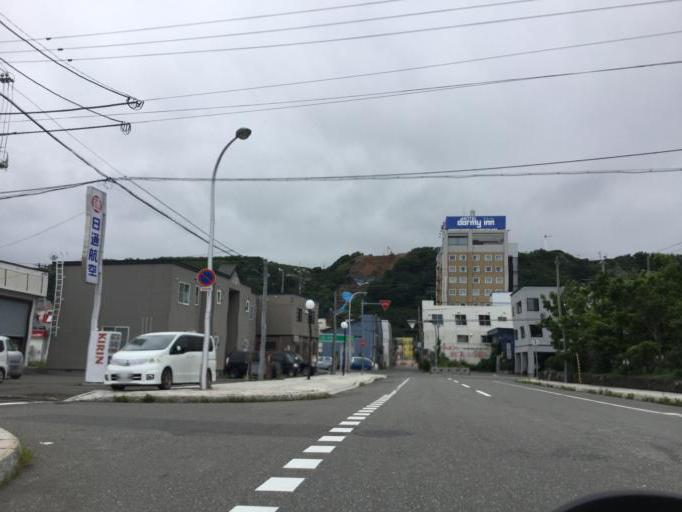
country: JP
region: Hokkaido
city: Wakkanai
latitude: 45.4186
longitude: 141.6771
